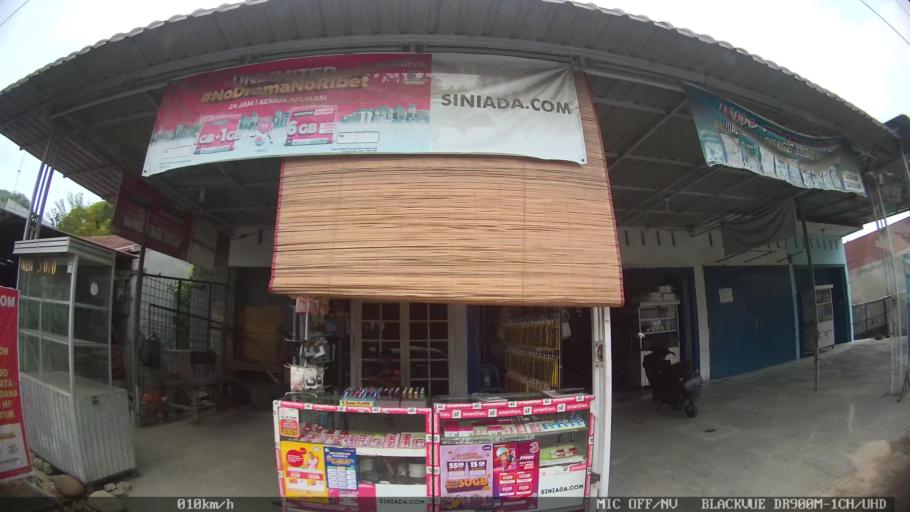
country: ID
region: North Sumatra
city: Sunggal
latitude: 3.6108
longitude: 98.6052
